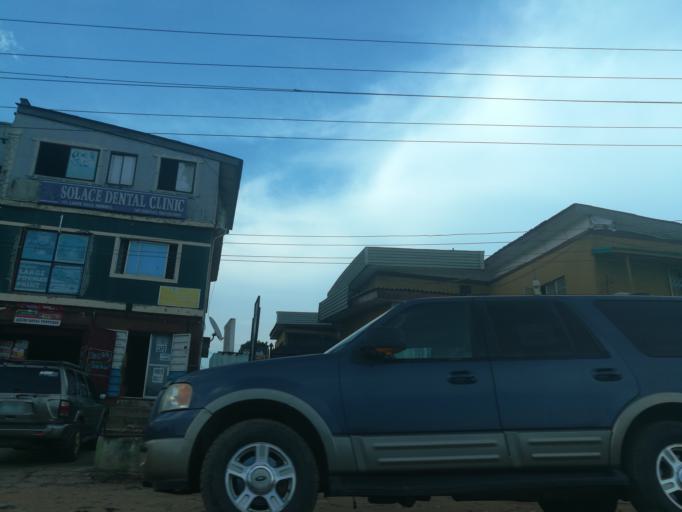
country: NG
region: Lagos
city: Ikorodu
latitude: 6.6246
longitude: 3.4941
